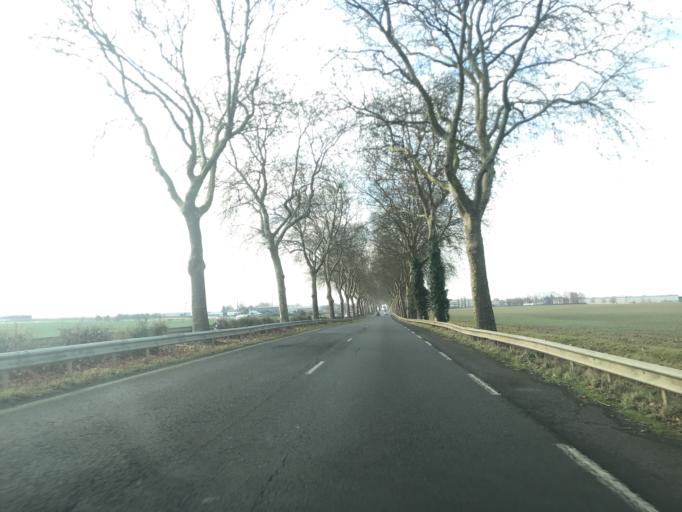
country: FR
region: Poitou-Charentes
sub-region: Departement des Deux-Sevres
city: Chauray
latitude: 46.3465
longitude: -0.3614
